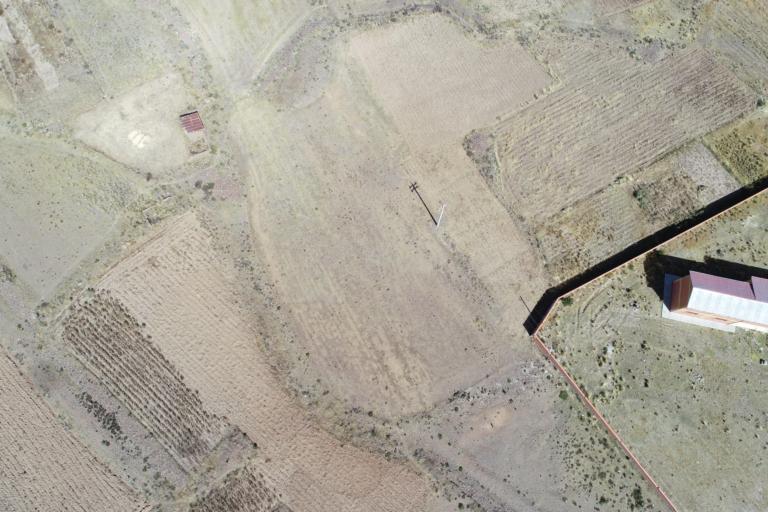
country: BO
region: La Paz
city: Achacachi
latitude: -15.8984
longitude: -68.9011
